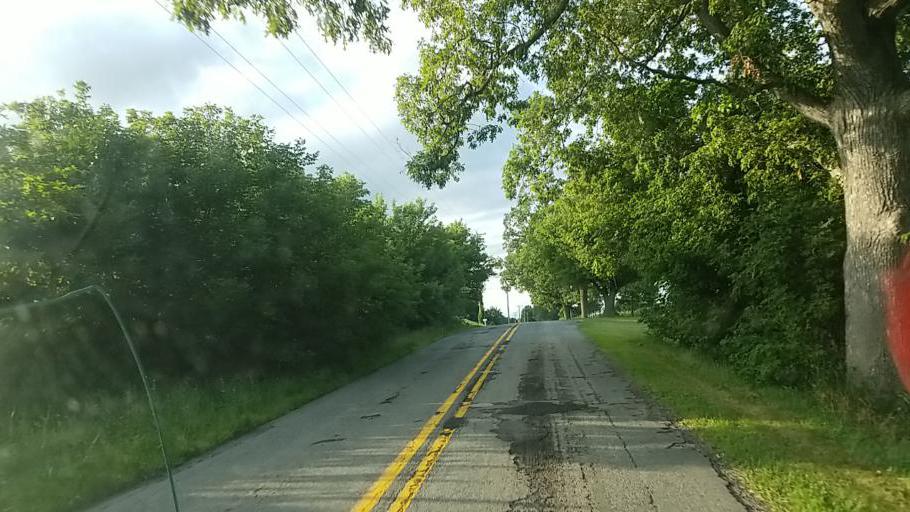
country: US
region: Michigan
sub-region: Montcalm County
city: Greenville
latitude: 43.2838
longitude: -85.3623
